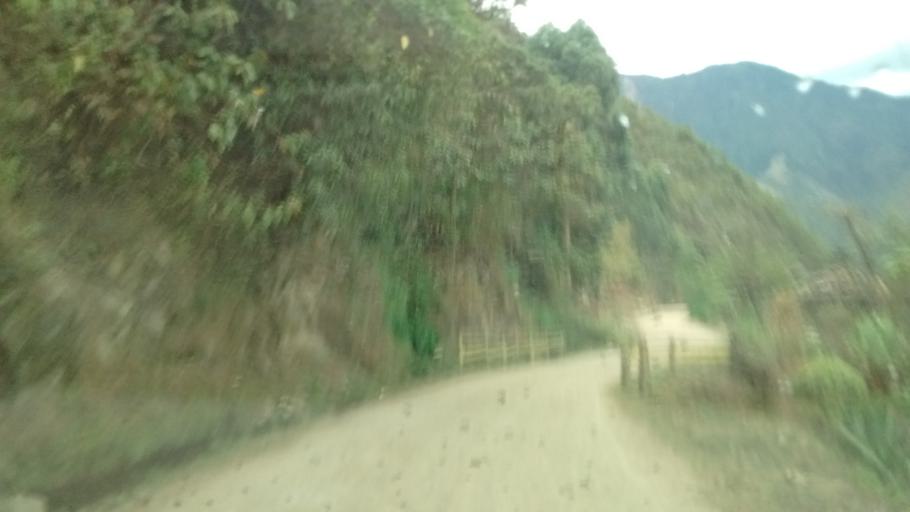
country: CO
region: Cauca
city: La Vega
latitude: 2.0402
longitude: -76.7970
